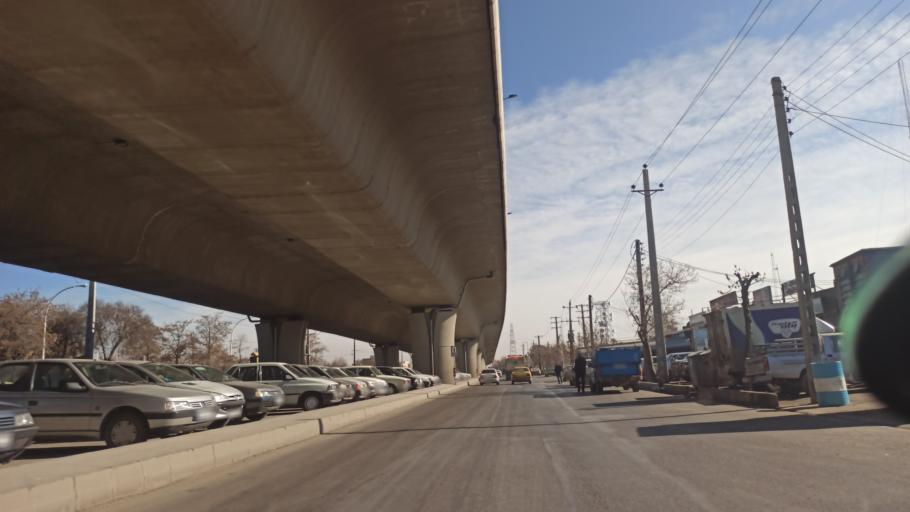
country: IR
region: Qazvin
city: Qazvin
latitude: 36.2556
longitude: 49.9981
